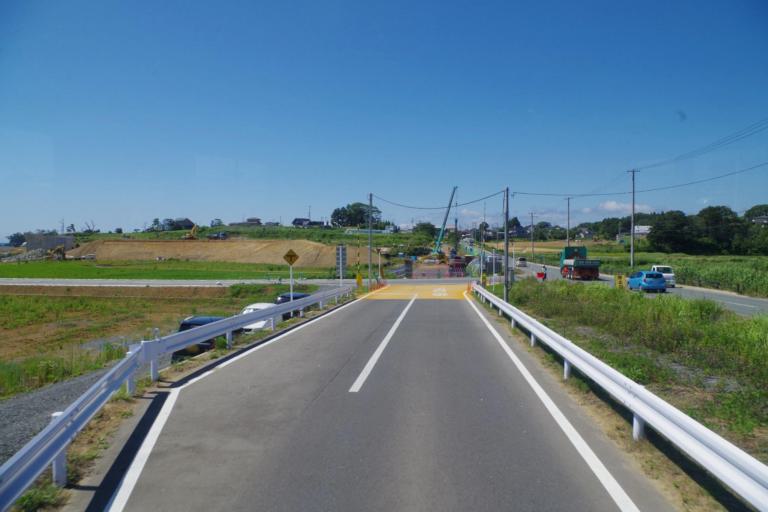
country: JP
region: Iwate
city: Ofunato
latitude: 38.8255
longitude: 141.5761
